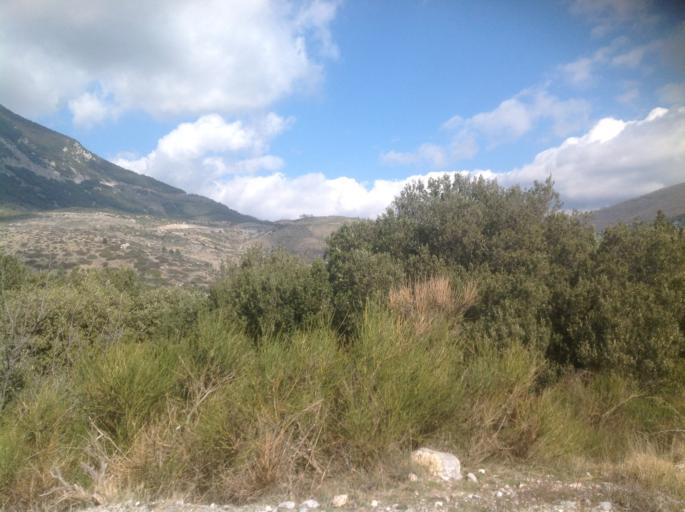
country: IT
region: Calabria
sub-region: Provincia di Cosenza
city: Civita
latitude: 39.8286
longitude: 16.3062
